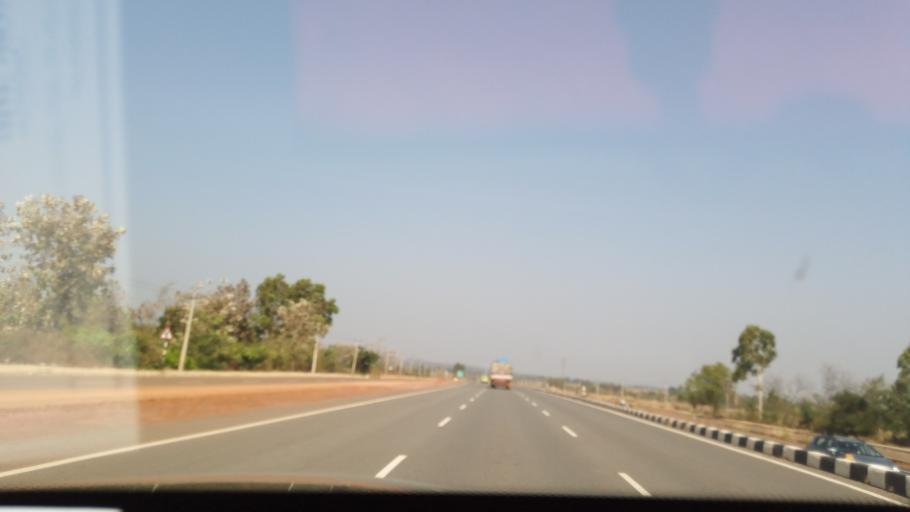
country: IN
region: Karnataka
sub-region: Haveri
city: Shiggaon
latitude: 15.0593
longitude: 75.1646
